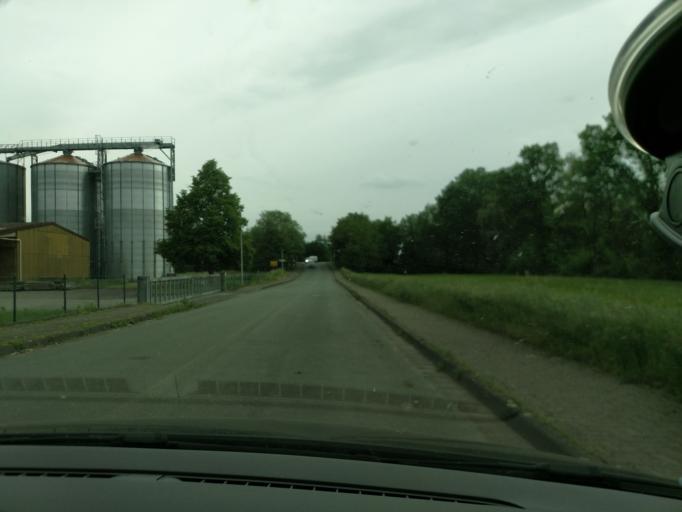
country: DE
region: Hesse
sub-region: Regierungsbezirk Kassel
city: Bad Arolsen
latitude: 51.3586
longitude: 8.9903
